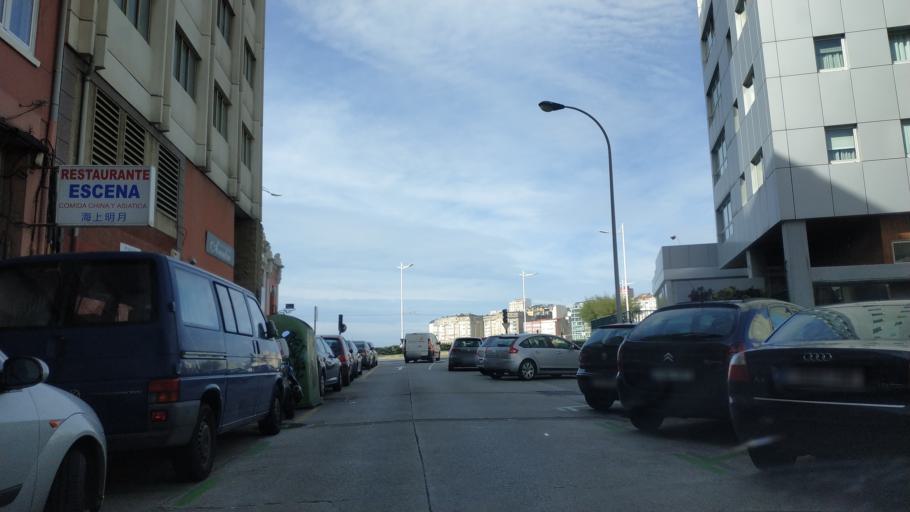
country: ES
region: Galicia
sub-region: Provincia da Coruna
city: A Coruna
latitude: 43.3722
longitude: -8.4024
